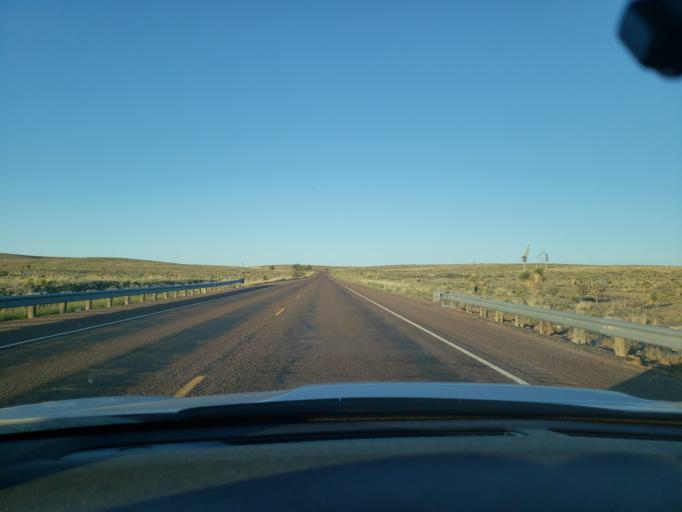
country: US
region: Texas
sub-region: El Paso County
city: Homestead Meadows South
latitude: 31.8350
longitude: -105.8519
